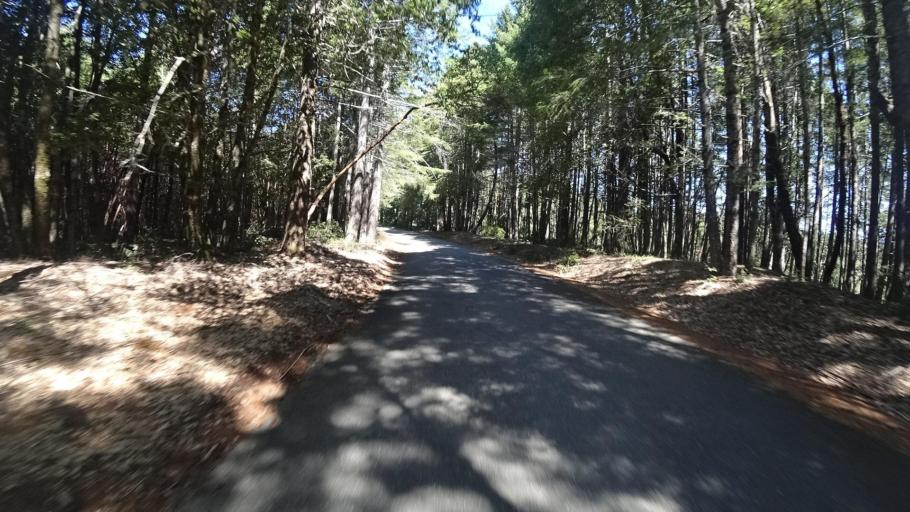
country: US
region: California
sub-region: Humboldt County
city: Redway
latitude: 40.1951
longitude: -124.0957
